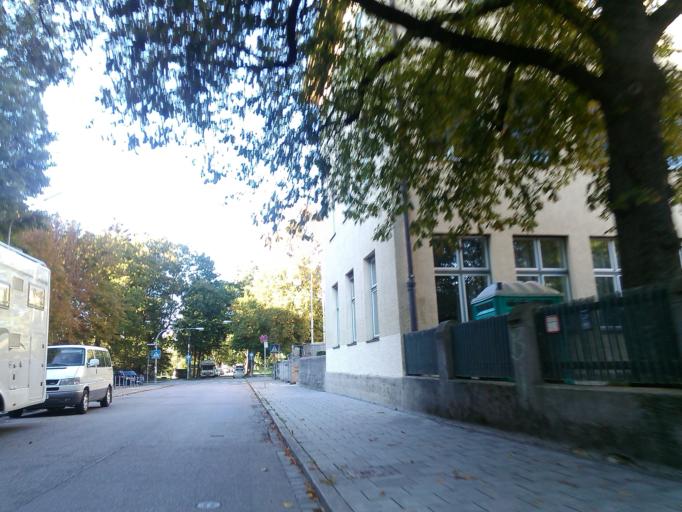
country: DE
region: Bavaria
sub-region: Upper Bavaria
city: Pasing
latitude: 48.1413
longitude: 11.4520
